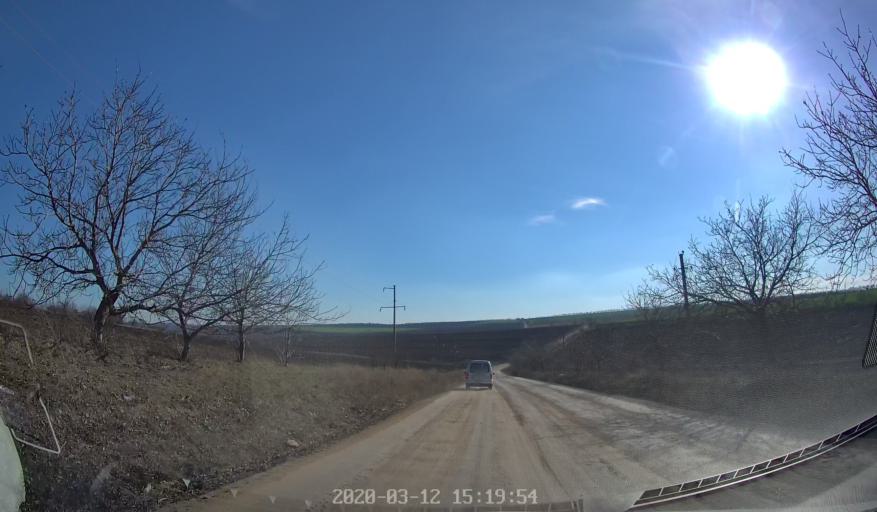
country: MD
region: Chisinau
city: Ciorescu
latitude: 47.2110
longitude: 28.9285
